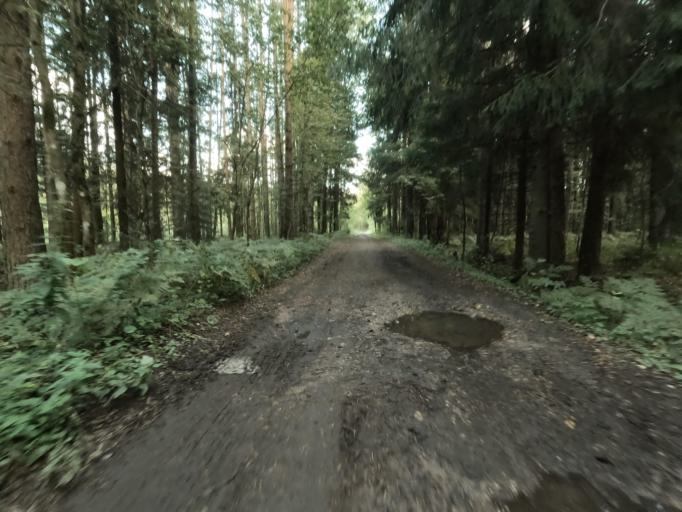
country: RU
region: Leningrad
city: Imeni Sverdlova
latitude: 59.8396
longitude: 30.7253
